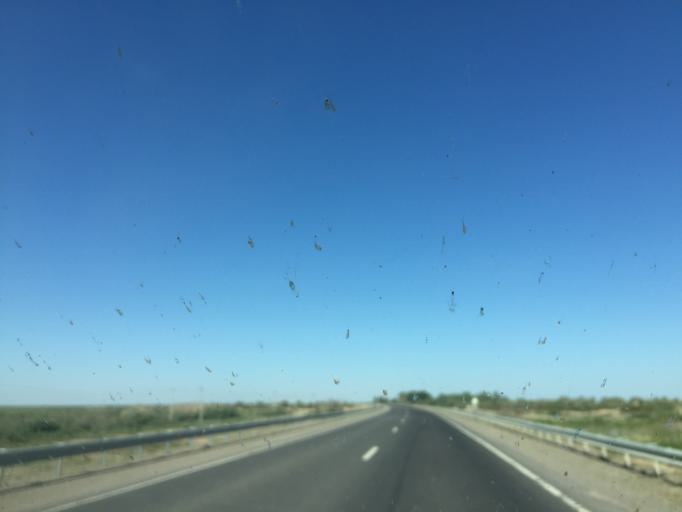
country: KZ
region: Qyzylorda
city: Terenozek
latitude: 44.8842
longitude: 64.8997
